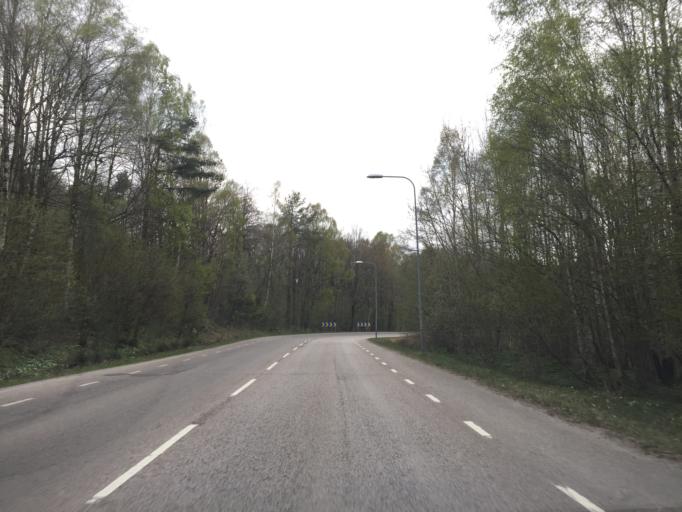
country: SE
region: Vaestra Goetaland
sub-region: Goteborg
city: Loevgaerdet
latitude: 57.8092
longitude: 12.0389
